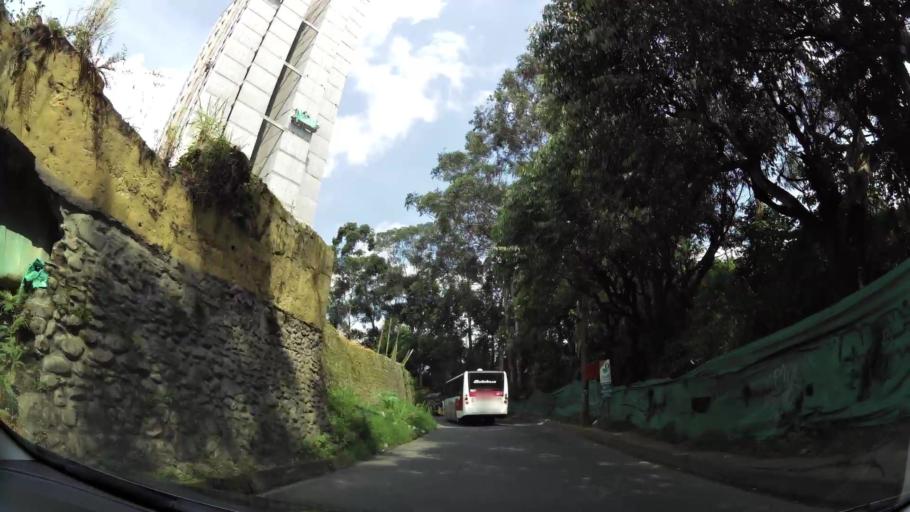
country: CO
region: Antioquia
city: La Estrella
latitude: 6.1759
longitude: -75.6357
